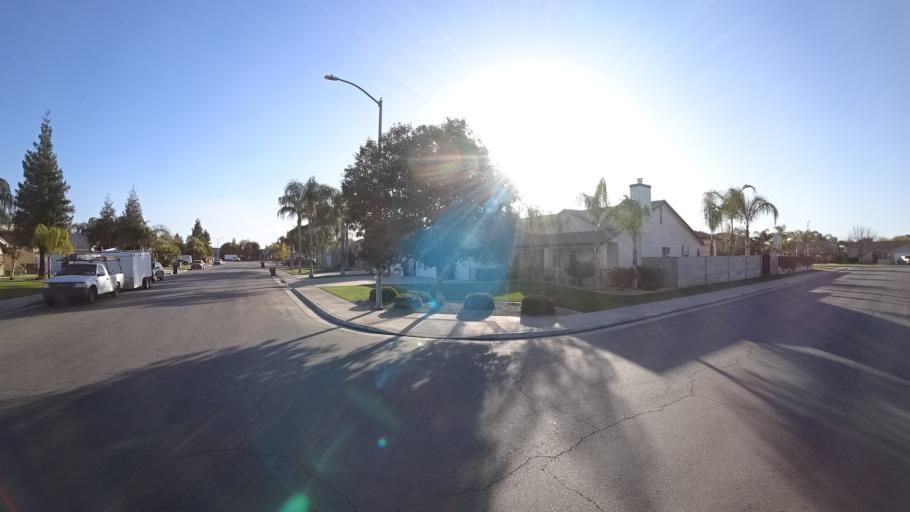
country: US
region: California
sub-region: Kern County
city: Greenfield
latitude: 35.2773
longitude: -119.0369
